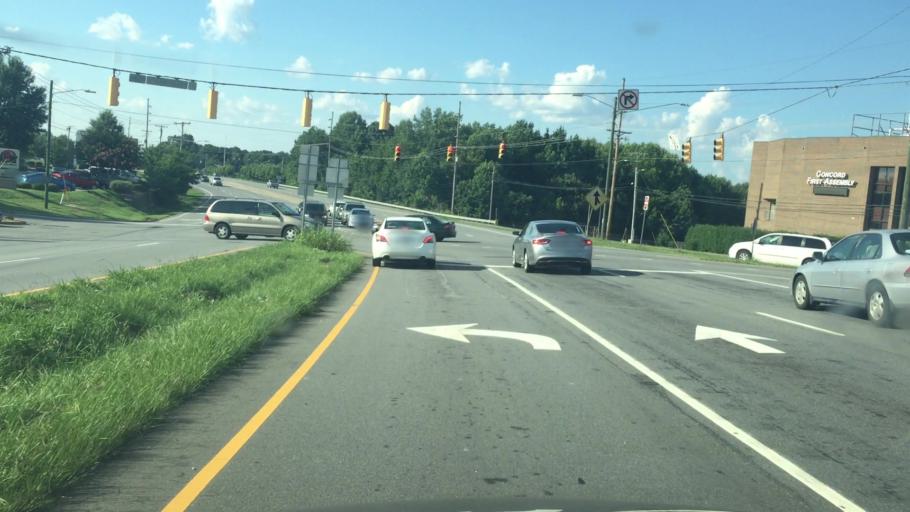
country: US
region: North Carolina
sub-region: Cabarrus County
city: Concord
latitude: 35.3995
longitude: -80.6084
